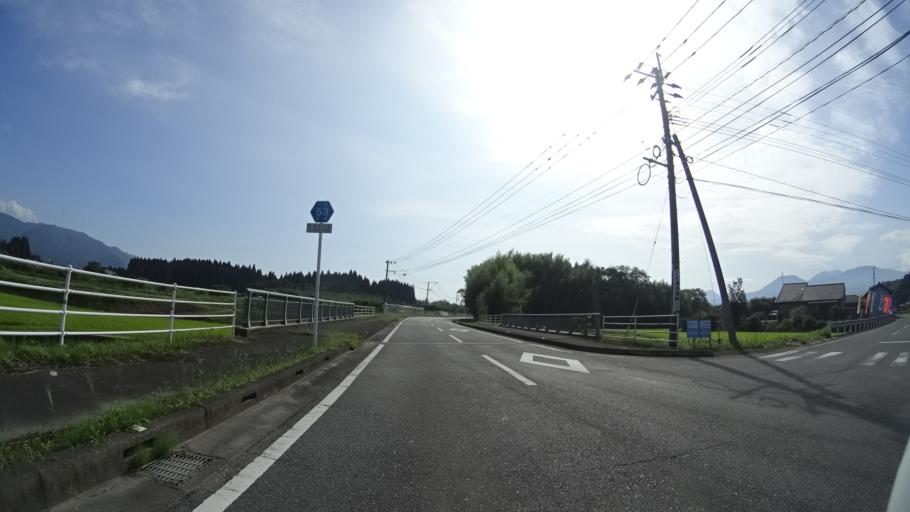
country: JP
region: Kagoshima
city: Okuchi-shinohara
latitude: 32.0414
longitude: 130.7880
